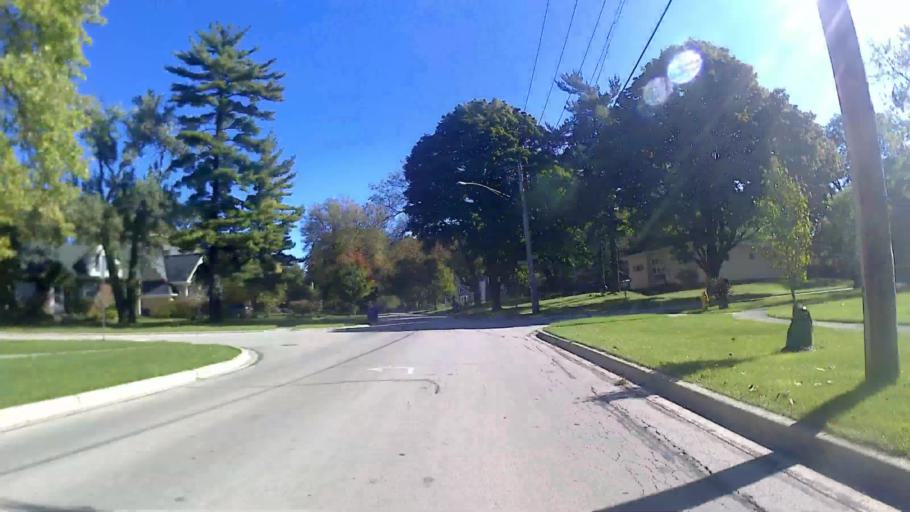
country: US
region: Illinois
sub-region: DuPage County
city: Wheaton
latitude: 41.8622
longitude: -88.0849
